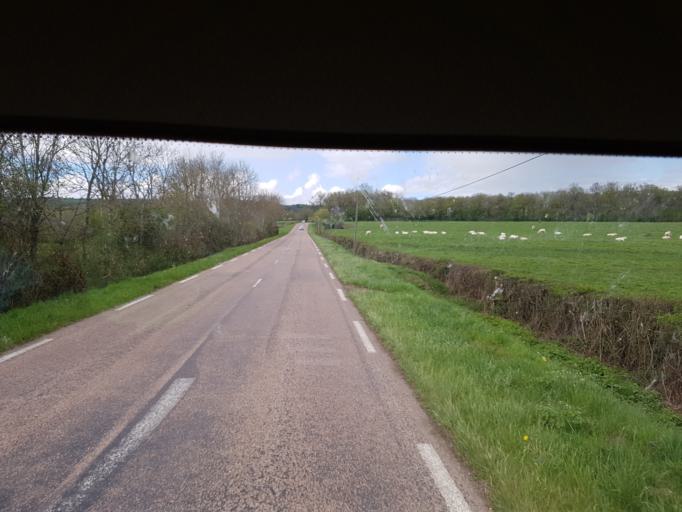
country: FR
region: Bourgogne
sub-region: Departement de Saone-et-Loire
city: Autun
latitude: 47.0274
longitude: 4.2846
